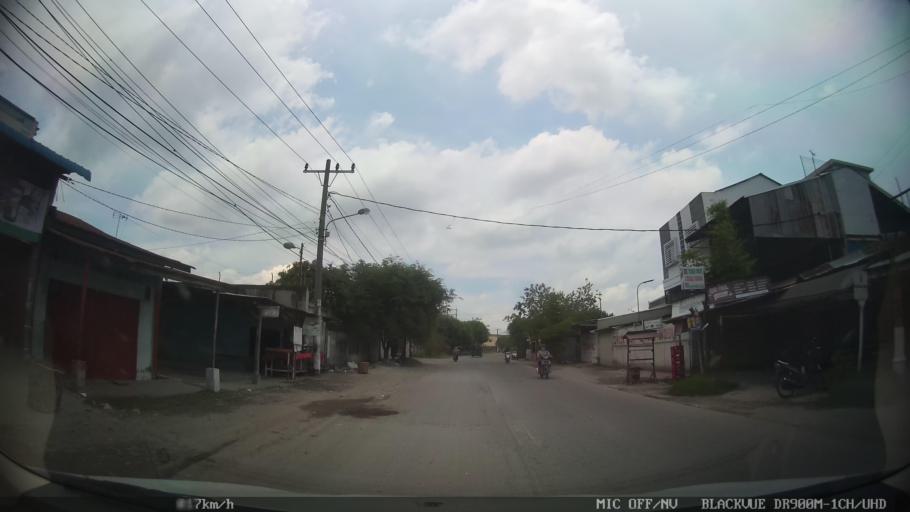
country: ID
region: North Sumatra
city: Labuhan Deli
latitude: 3.6762
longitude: 98.6734
